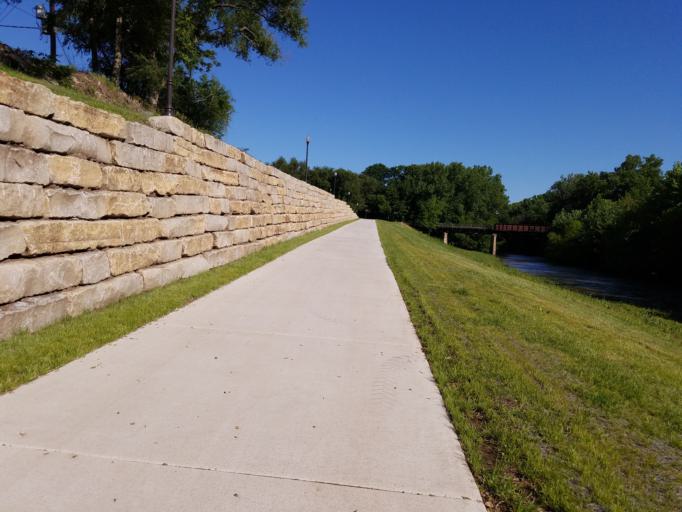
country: US
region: Kansas
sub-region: Morris County
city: Council Grove
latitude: 38.6613
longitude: -96.4878
